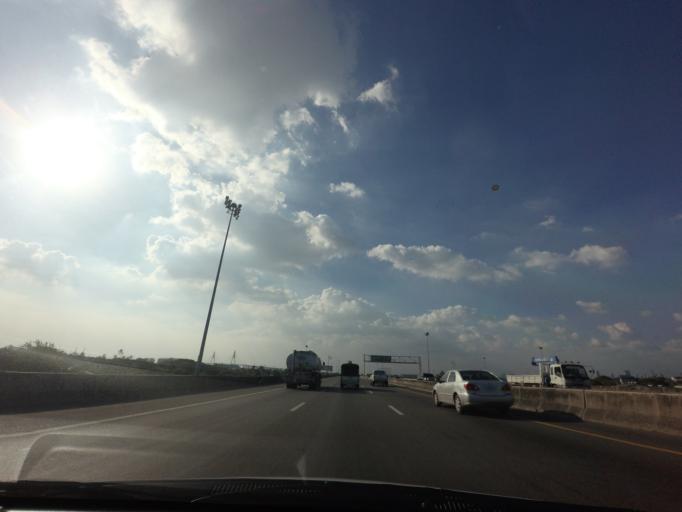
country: TH
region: Samut Prakan
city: Phra Samut Chedi
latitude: 13.6342
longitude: 100.5687
